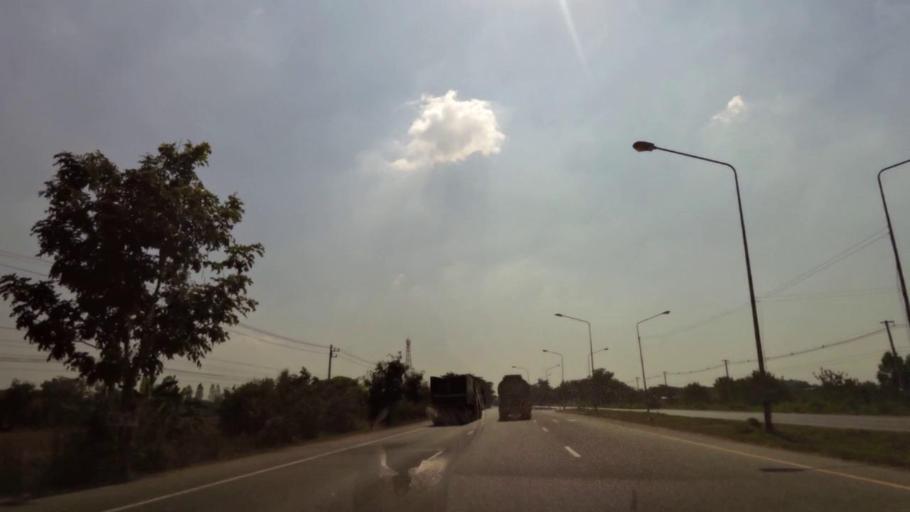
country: TH
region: Phichit
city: Bueng Na Rang
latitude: 16.1623
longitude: 100.1260
